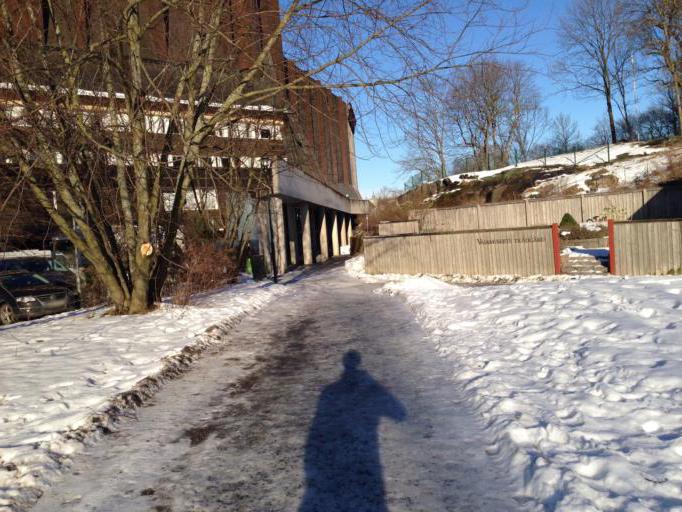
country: SE
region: Stockholm
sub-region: Stockholms Kommun
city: OEstermalm
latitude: 59.3275
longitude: 18.0926
